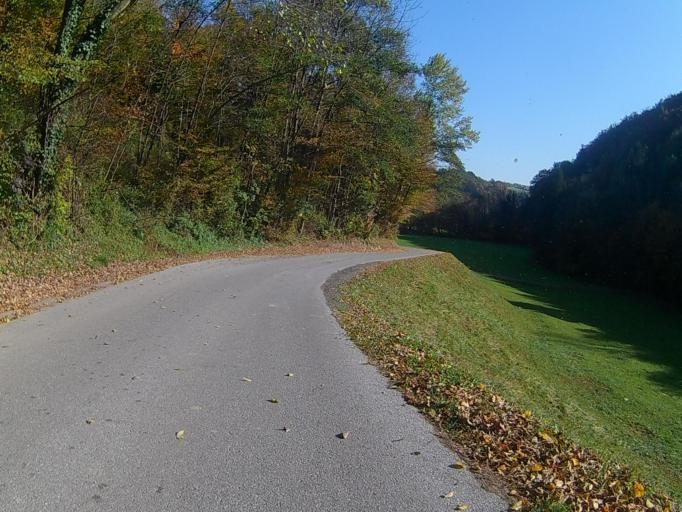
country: SI
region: Race-Fram
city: Morje
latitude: 46.4479
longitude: 15.5906
